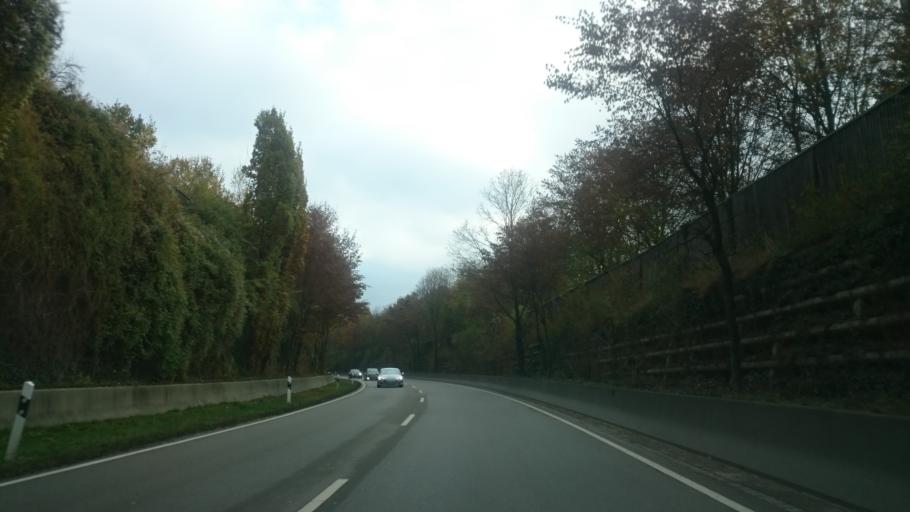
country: DE
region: Bavaria
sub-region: Swabia
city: Guenzburg
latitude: 48.4580
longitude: 10.2860
